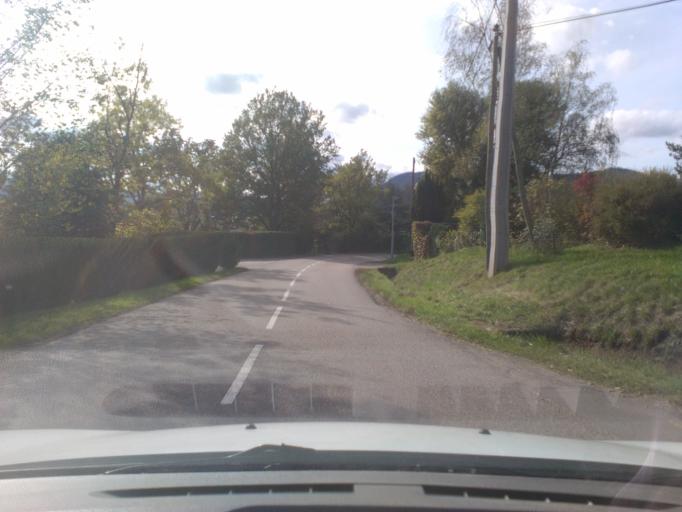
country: FR
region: Lorraine
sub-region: Departement des Vosges
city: Sainte-Marguerite
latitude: 48.2886
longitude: 6.9743
